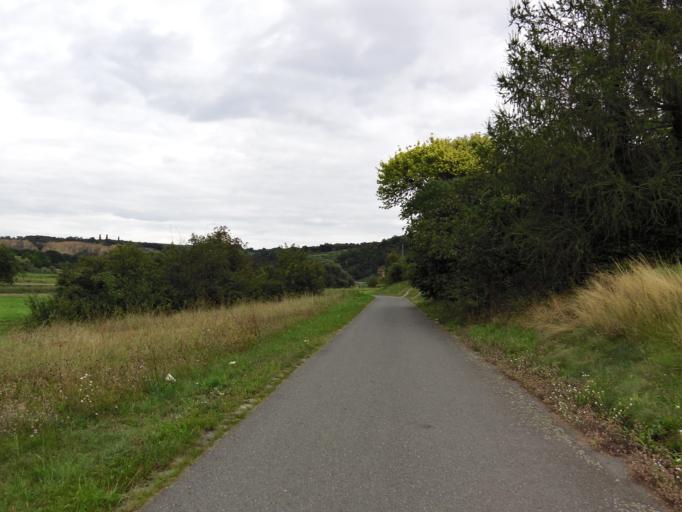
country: DE
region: Saxony
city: Weissig
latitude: 51.2245
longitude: 13.4206
